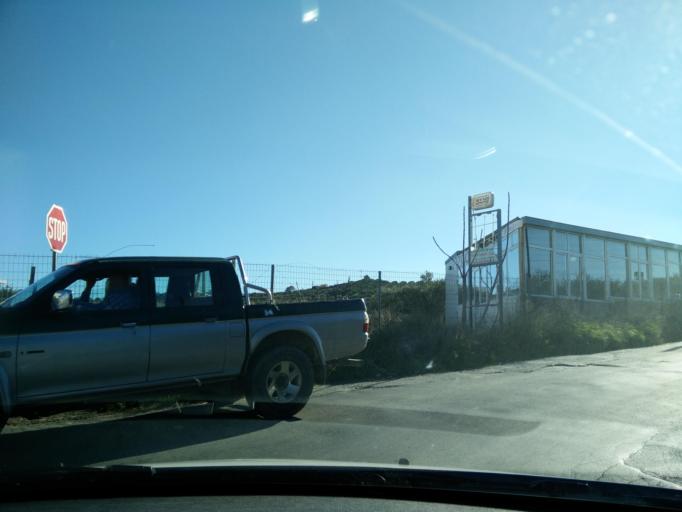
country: GR
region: Crete
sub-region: Nomos Irakleiou
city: Arkalochori
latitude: 35.1378
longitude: 25.2626
